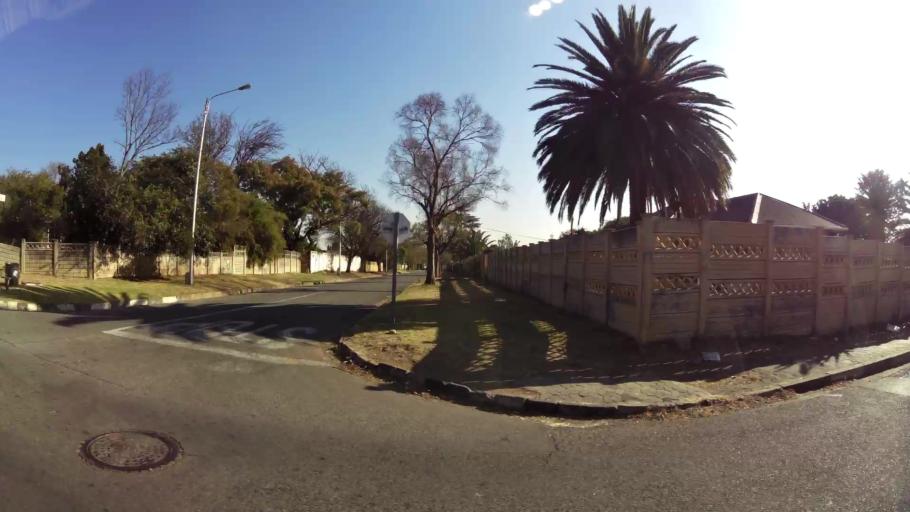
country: ZA
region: Gauteng
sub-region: City of Johannesburg Metropolitan Municipality
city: Modderfontein
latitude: -26.1387
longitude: 28.1578
